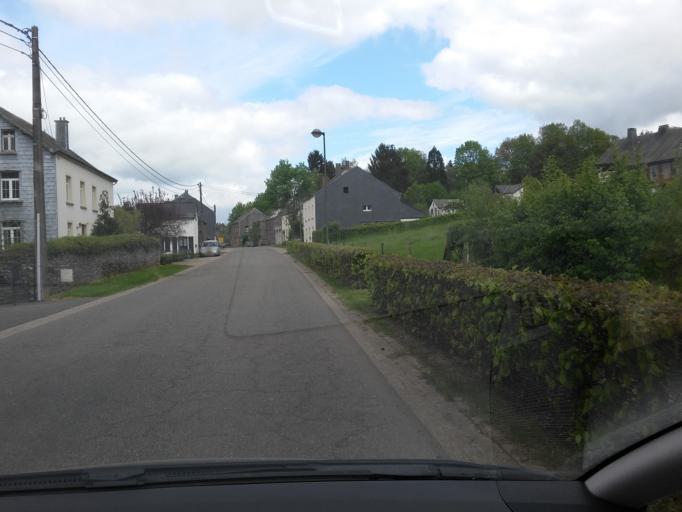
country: BE
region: Wallonia
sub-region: Province du Luxembourg
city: Herbeumont
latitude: 49.7782
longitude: 5.2394
